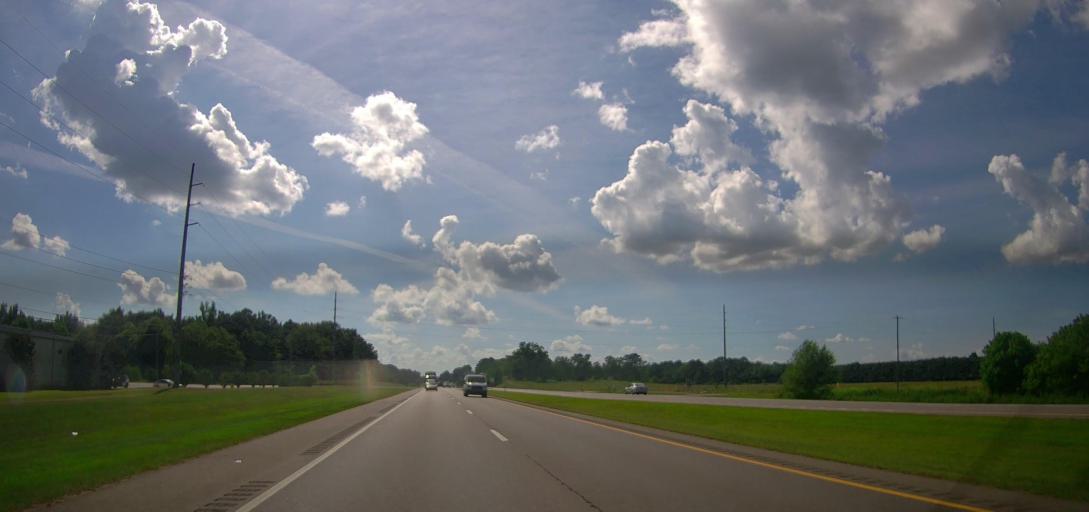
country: US
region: Alabama
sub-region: Tuscaloosa County
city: Northport
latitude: 33.2334
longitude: -87.6327
